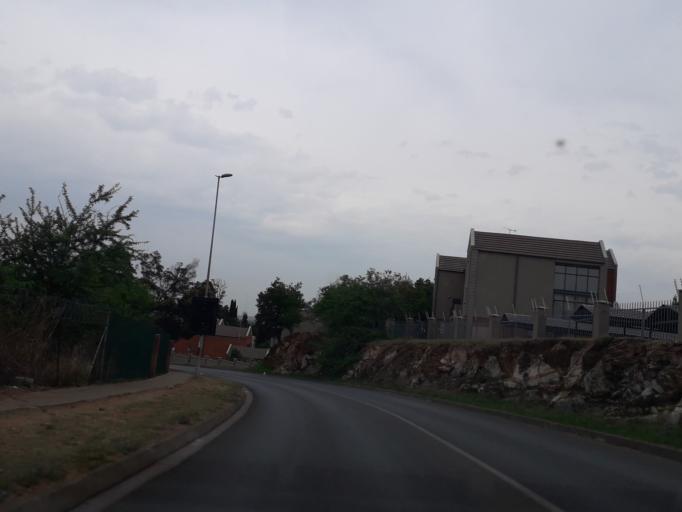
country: ZA
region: Gauteng
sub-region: City of Johannesburg Metropolitan Municipality
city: Johannesburg
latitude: -26.1274
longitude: 27.9814
